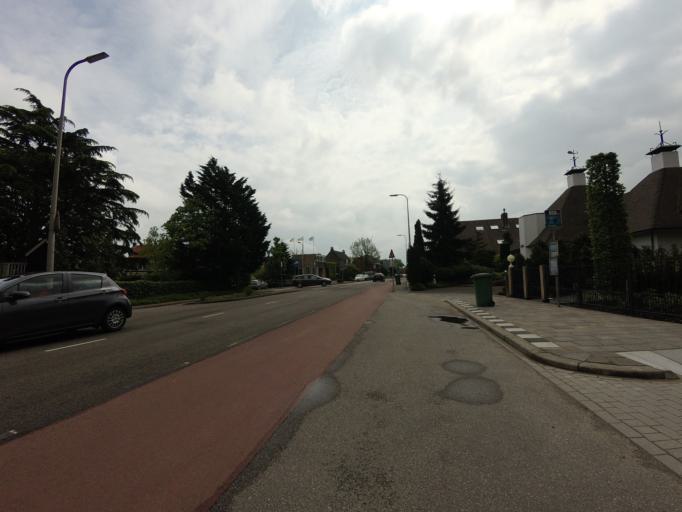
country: NL
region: South Holland
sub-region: Gemeente Ridderkerk
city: Ridderkerk
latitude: 51.8514
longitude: 4.5938
